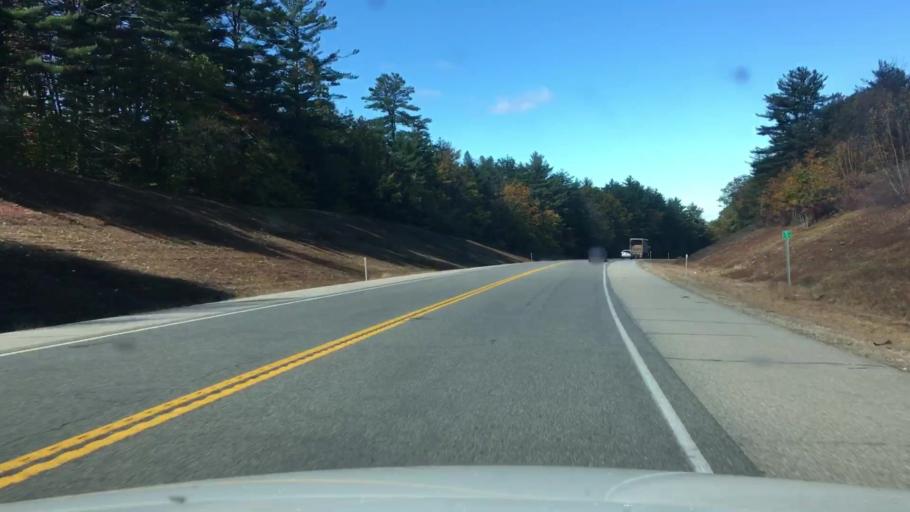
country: US
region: New Hampshire
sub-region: Carroll County
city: Ossipee
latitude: 43.7661
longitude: -71.1575
